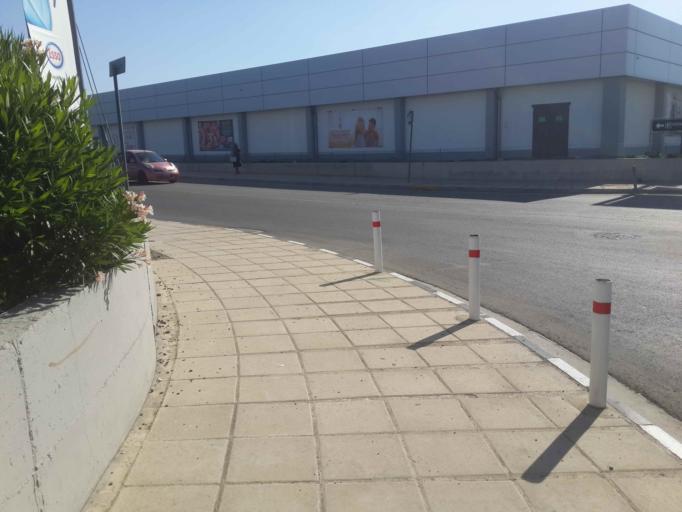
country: CY
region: Lefkosia
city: Nicosia
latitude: 35.1467
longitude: 33.3278
